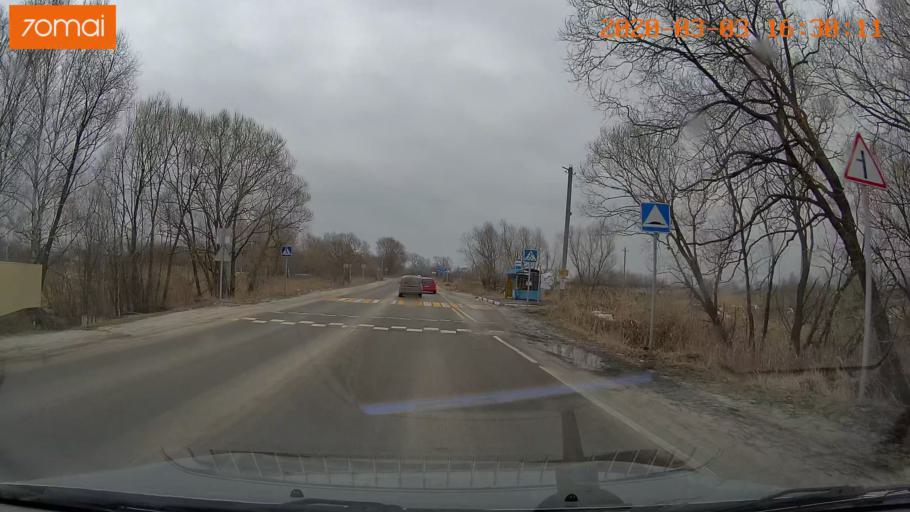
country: RU
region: Moskovskaya
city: Konobeyevo
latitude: 55.4340
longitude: 38.7093
